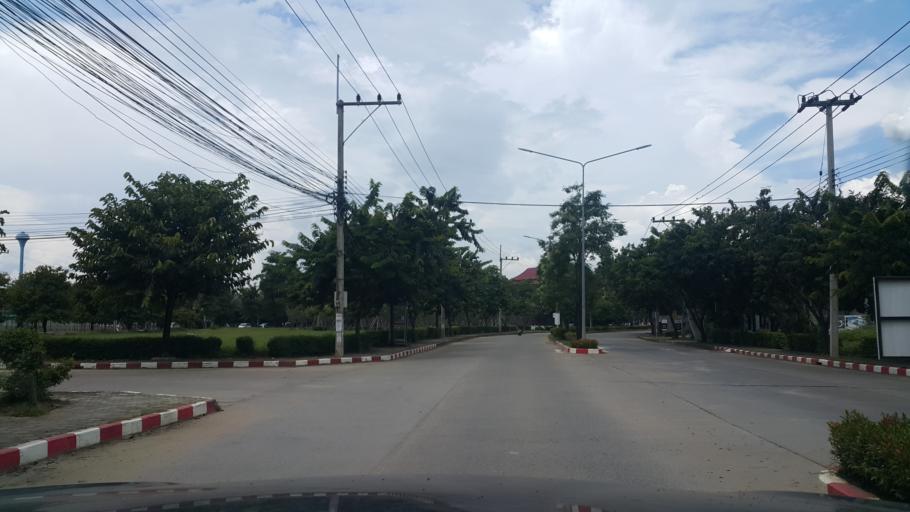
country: TH
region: Chiang Mai
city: Chiang Mai
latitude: 18.8041
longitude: 99.0246
